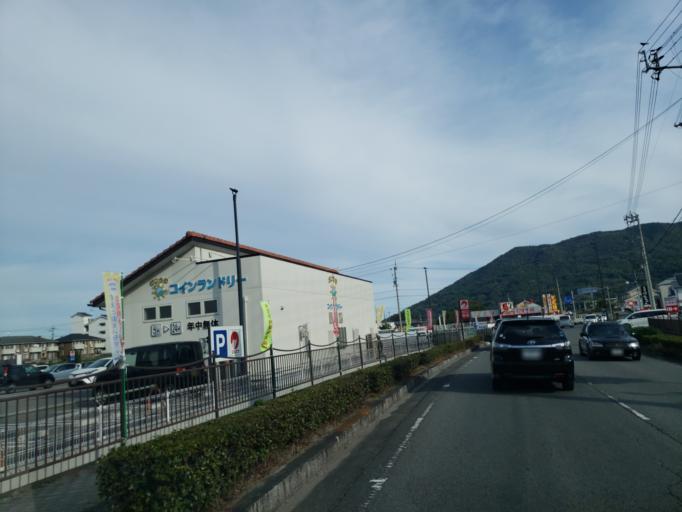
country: JP
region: Tokushima
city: Wakimachi
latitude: 34.0634
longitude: 134.1662
